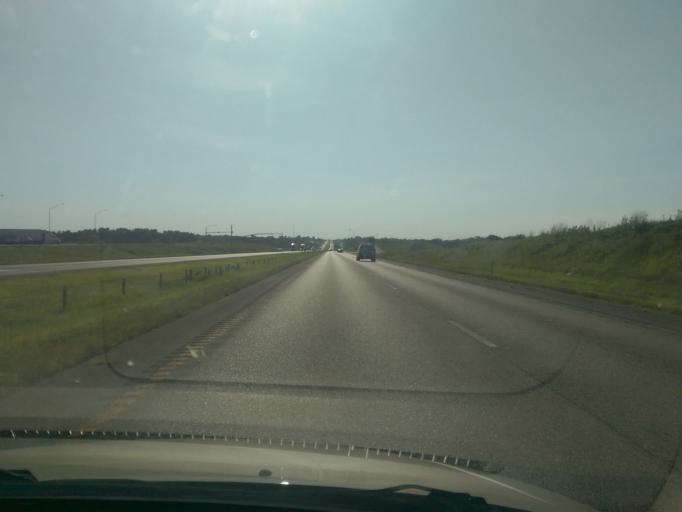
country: US
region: Missouri
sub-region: Lafayette County
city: Odessa
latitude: 39.0044
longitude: -93.8524
